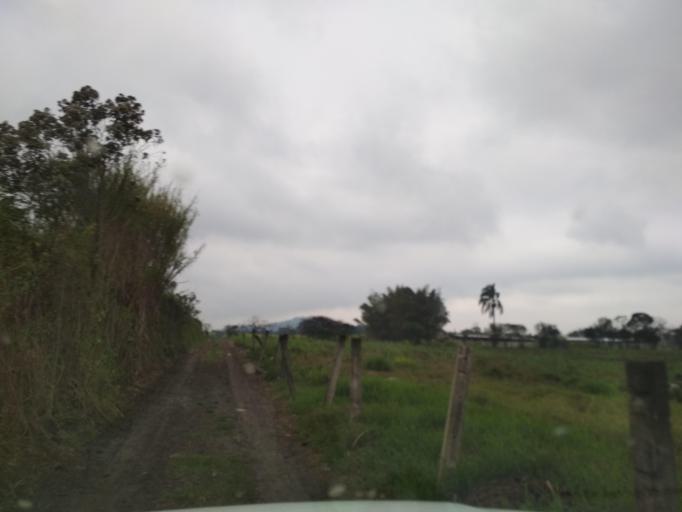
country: MX
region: Veracruz
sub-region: Cordoba
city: Veinte de Noviembre
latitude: 18.8691
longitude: -96.9561
